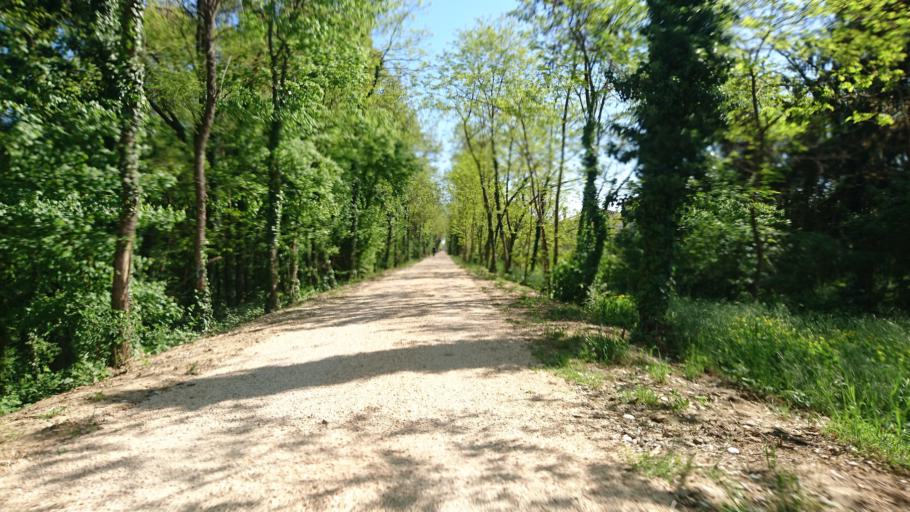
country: IT
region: Veneto
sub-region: Provincia di Treviso
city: Castagnole
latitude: 45.6583
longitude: 12.1945
